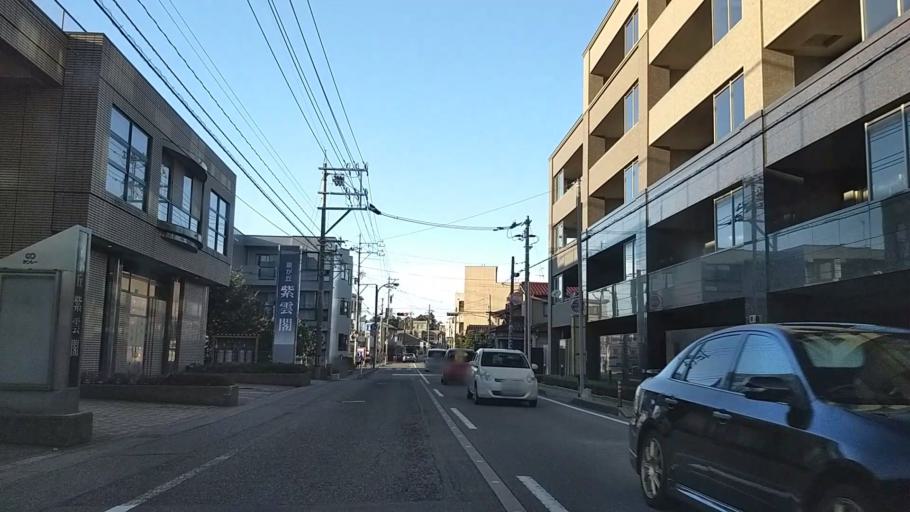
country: JP
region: Ishikawa
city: Nonoichi
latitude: 36.5471
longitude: 136.6491
